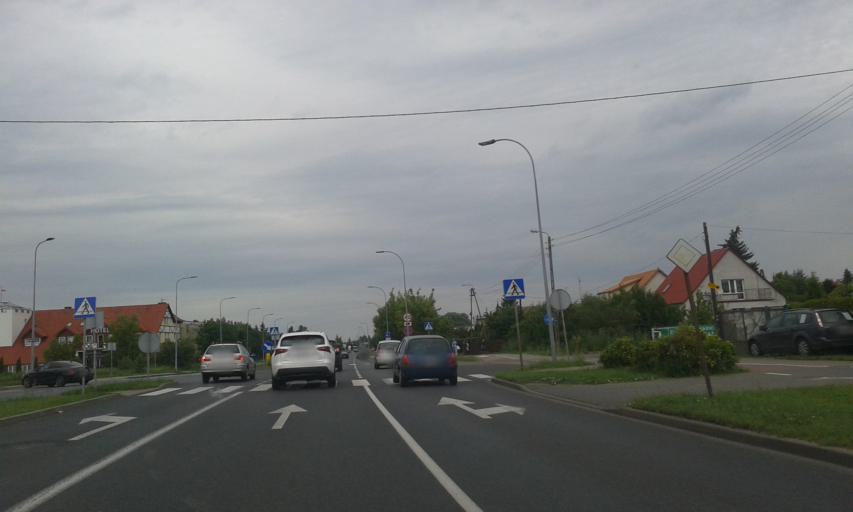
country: PL
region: Kujawsko-Pomorskie
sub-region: Bydgoszcz
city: Bydgoszcz
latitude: 53.1401
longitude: 17.9631
